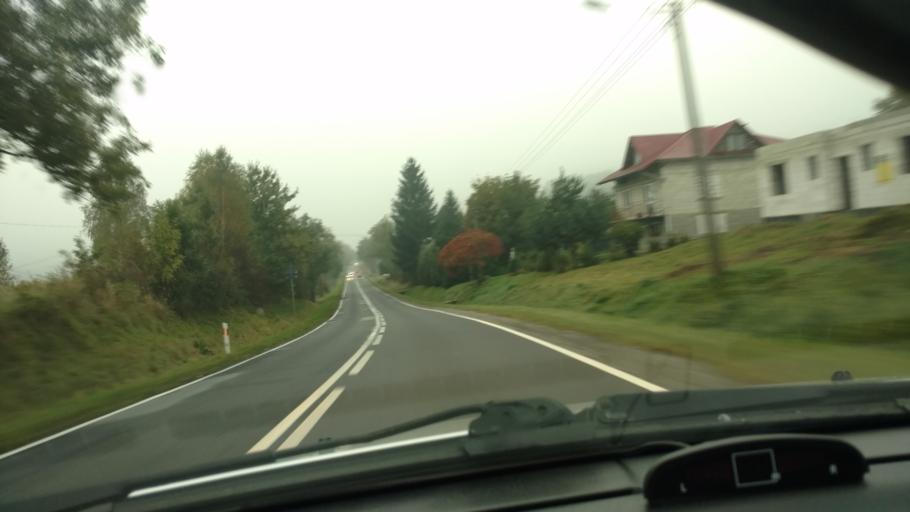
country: PL
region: Subcarpathian Voivodeship
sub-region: Powiat strzyzowski
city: Frysztak
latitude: 49.8615
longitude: 21.6256
